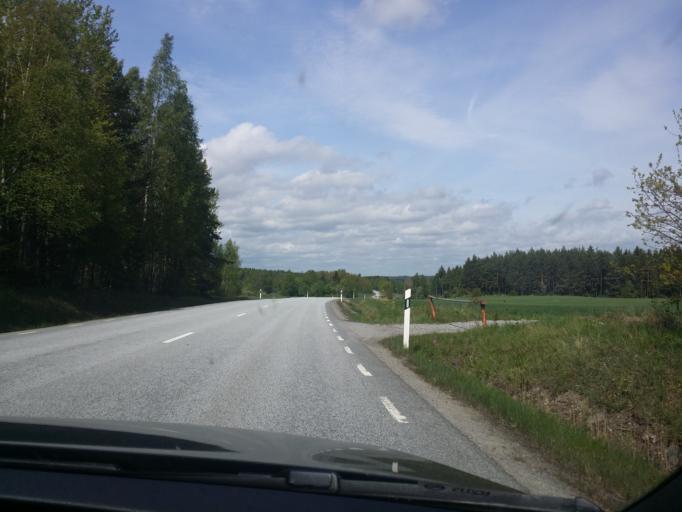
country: SE
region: Uppsala
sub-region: Habo Kommun
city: Balsta
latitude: 59.6436
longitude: 17.5687
